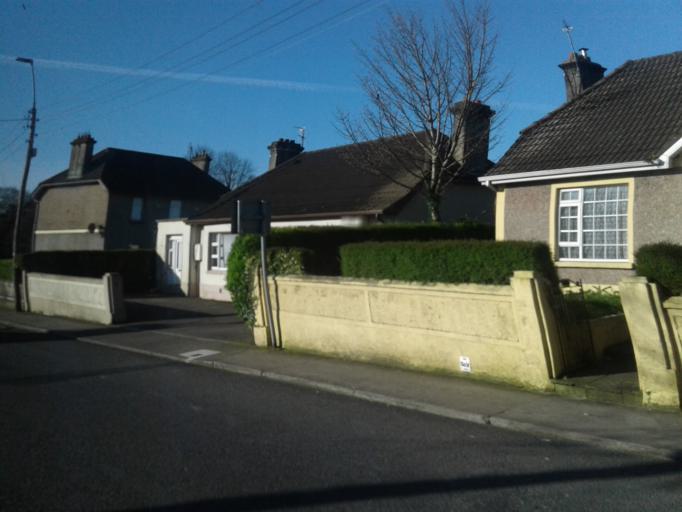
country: IE
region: Munster
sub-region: An Clar
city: Ennis
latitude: 52.8367
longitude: -8.9830
